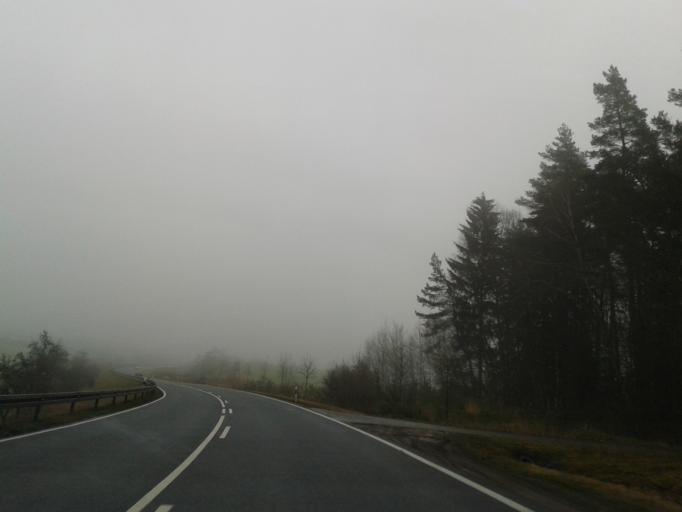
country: DE
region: Bavaria
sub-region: Regierungsbezirk Unterfranken
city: Pfarrweisach
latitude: 50.1916
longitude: 10.7417
